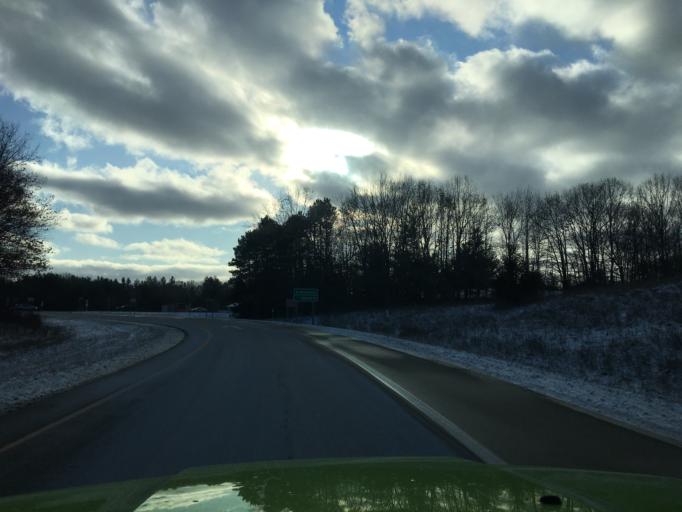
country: US
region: Michigan
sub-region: Kent County
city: Cedar Springs
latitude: 43.1771
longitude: -85.5780
